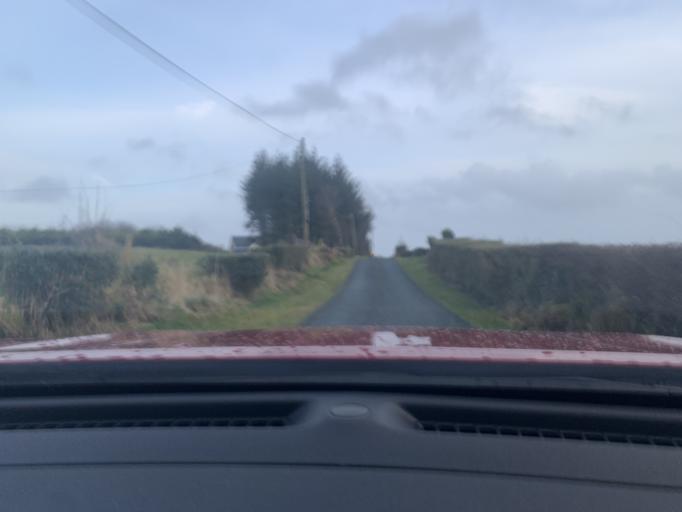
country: IE
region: Connaught
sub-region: Roscommon
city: Ballaghaderreen
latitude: 53.9492
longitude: -8.5132
